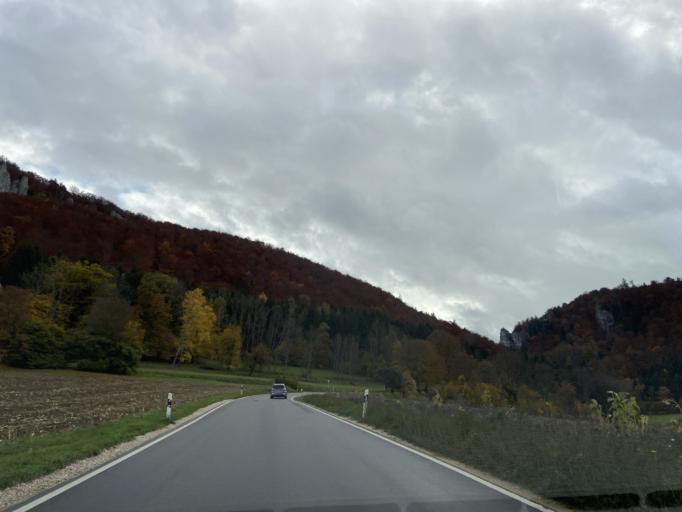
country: DE
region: Baden-Wuerttemberg
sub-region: Tuebingen Region
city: Schwenningen
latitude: 48.0790
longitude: 9.0343
